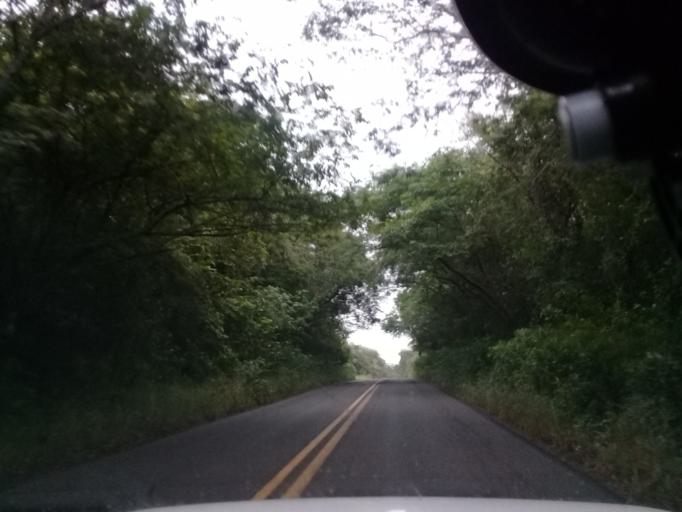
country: MX
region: Veracruz
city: Platon Sanchez
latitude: 21.2280
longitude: -98.3717
